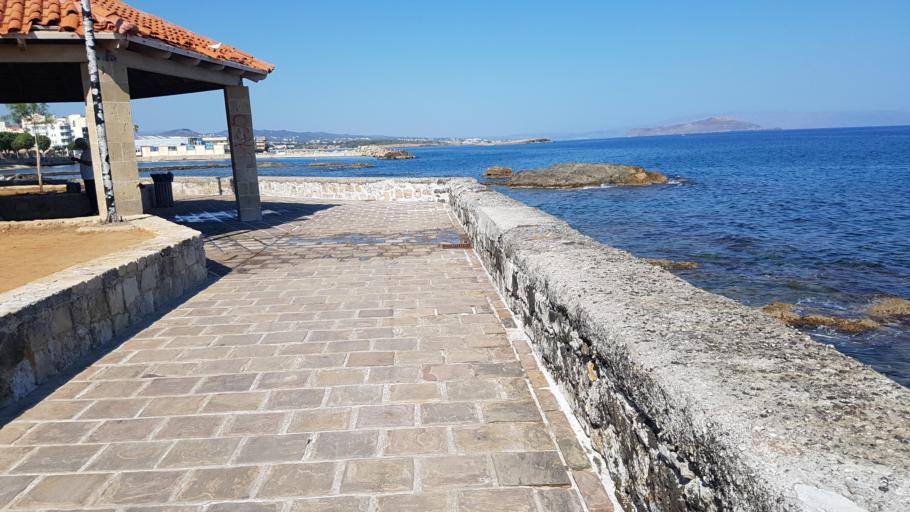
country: GR
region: Crete
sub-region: Nomos Chanias
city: Chania
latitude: 35.5191
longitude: 24.0139
